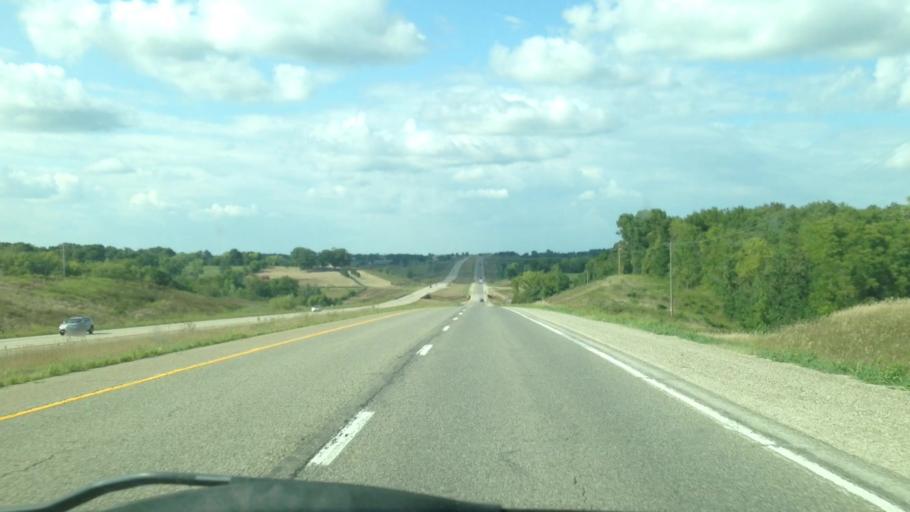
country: US
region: Iowa
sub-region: Henry County
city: Mount Pleasant
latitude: 40.8522
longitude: -91.5646
